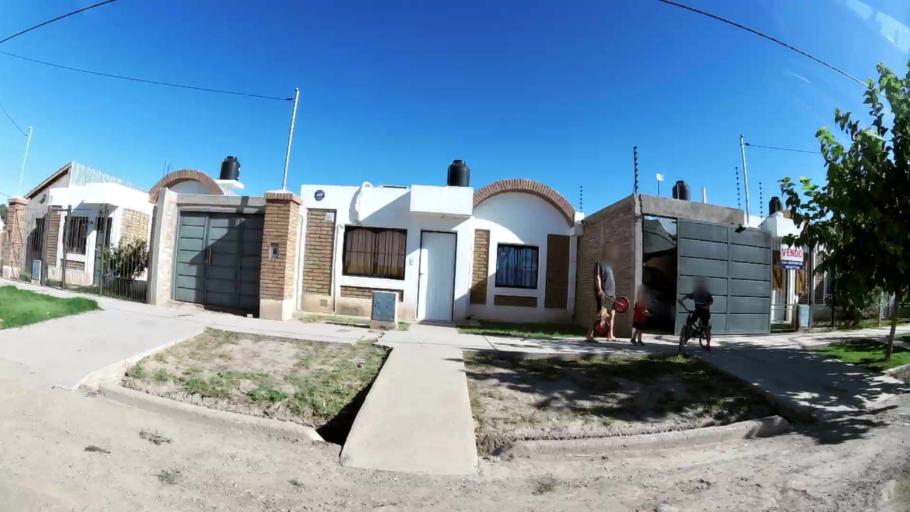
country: AR
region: Mendoza
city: Las Heras
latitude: -32.8452
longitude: -68.8300
